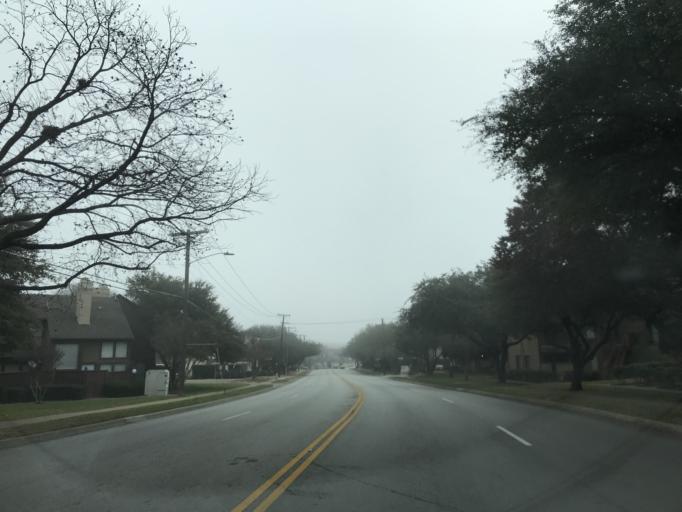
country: US
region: Texas
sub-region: Tarrant County
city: Arlington
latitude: 32.7743
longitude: -97.0680
